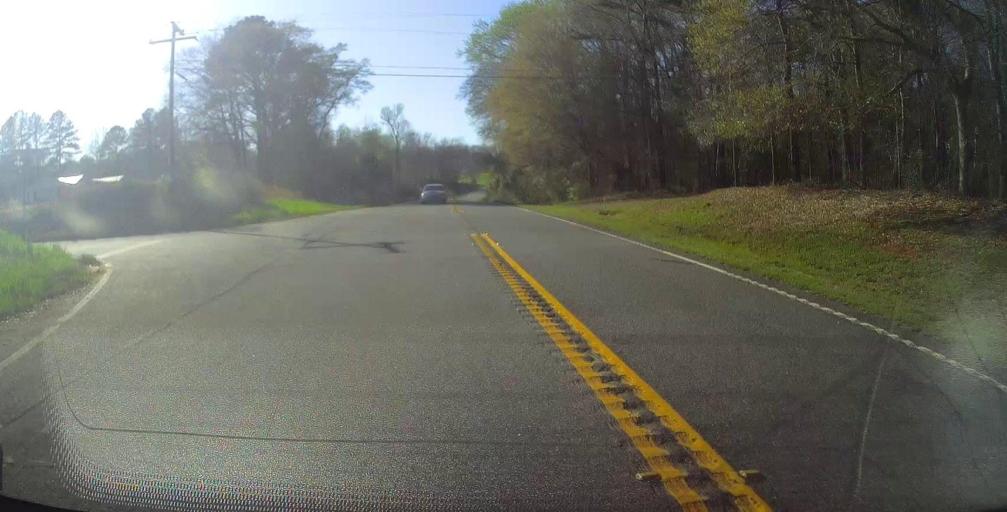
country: US
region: Georgia
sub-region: Macon County
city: Marshallville
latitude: 32.4398
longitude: -83.8850
